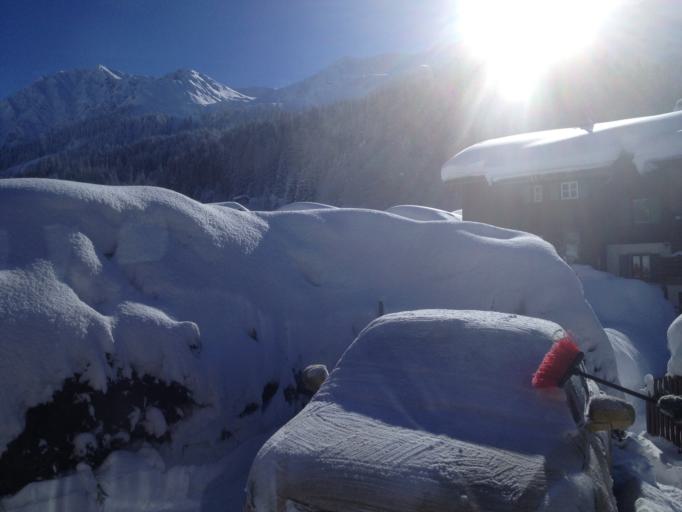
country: CH
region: Grisons
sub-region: Praettigau/Davos District
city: Klosters Serneus
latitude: 46.8614
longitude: 9.9009
